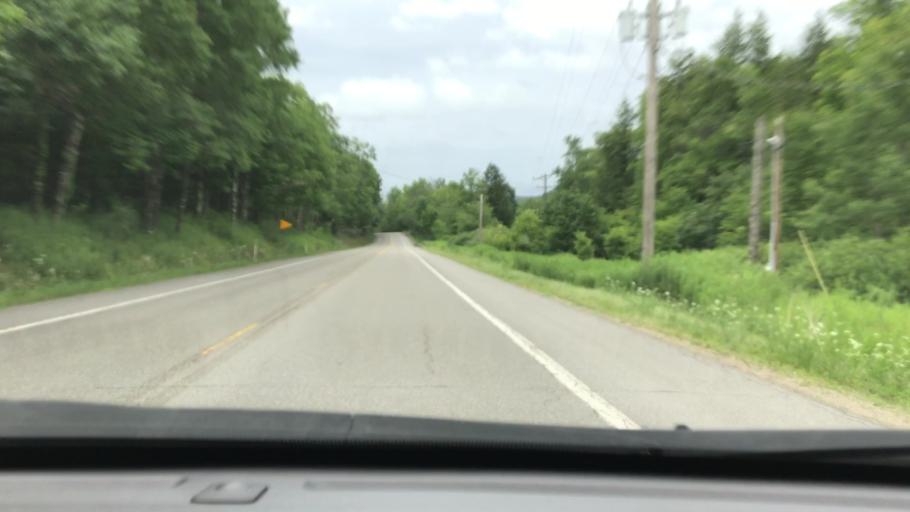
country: US
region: Pennsylvania
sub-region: McKean County
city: Bradford
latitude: 41.8520
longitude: -78.6772
